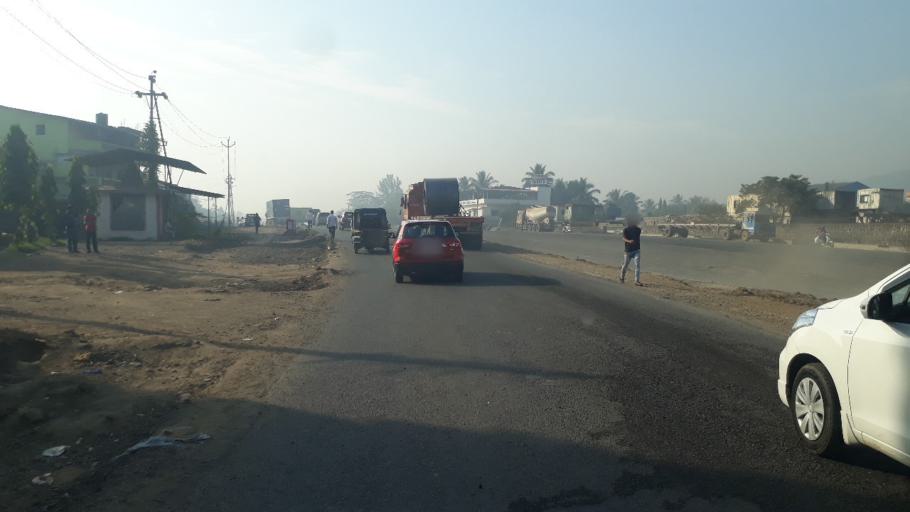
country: IN
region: Maharashtra
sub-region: Raigarh
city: Kalundri
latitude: 18.9584
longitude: 73.1309
